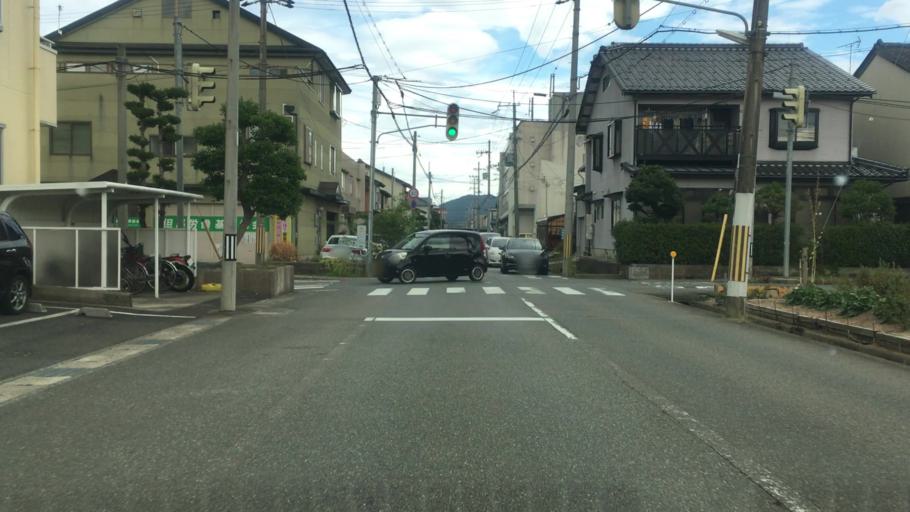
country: JP
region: Hyogo
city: Toyooka
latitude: 35.5487
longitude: 134.8130
